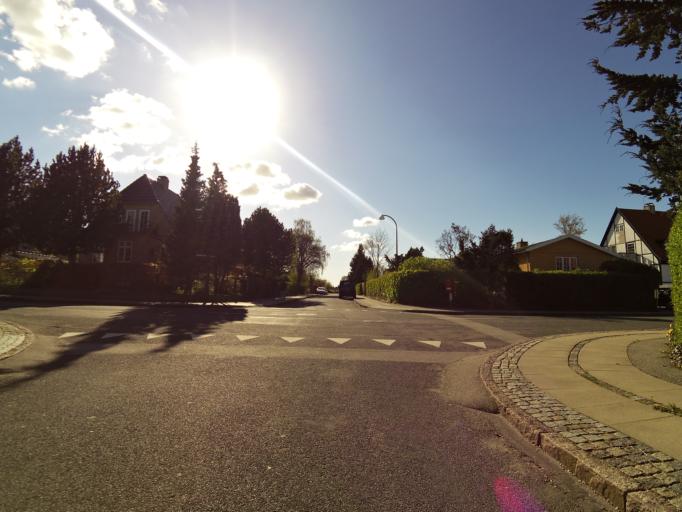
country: DK
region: Capital Region
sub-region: Lyngby-Tarbaek Kommune
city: Kongens Lyngby
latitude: 55.7355
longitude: 12.5286
